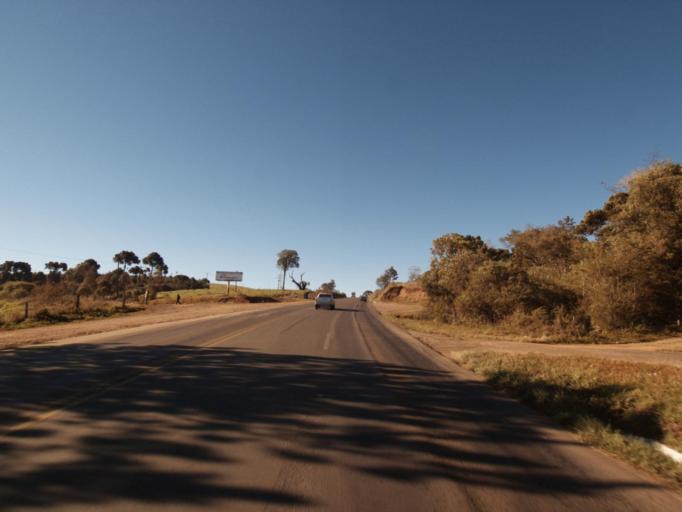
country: BR
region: Santa Catarina
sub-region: Concordia
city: Concordia
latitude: -26.8900
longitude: -51.9864
